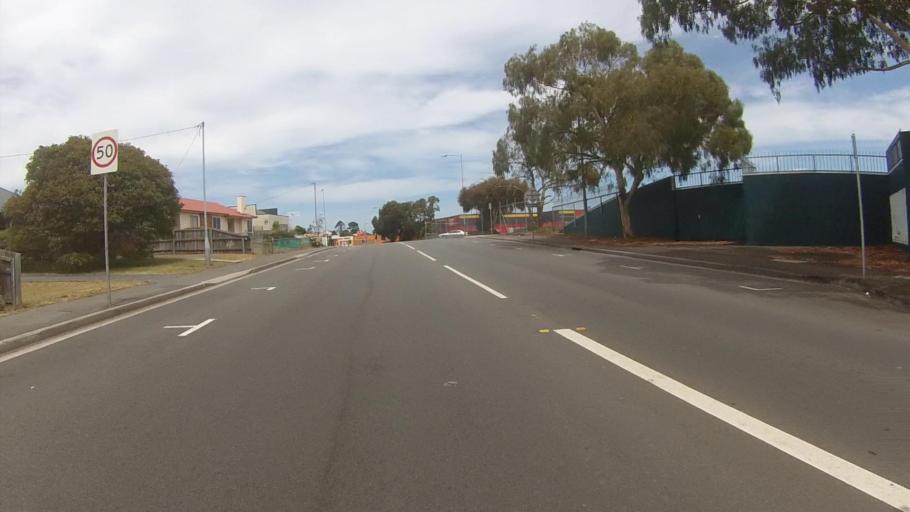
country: AU
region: Tasmania
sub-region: Clarence
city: Bellerive
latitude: -42.8637
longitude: 147.3717
